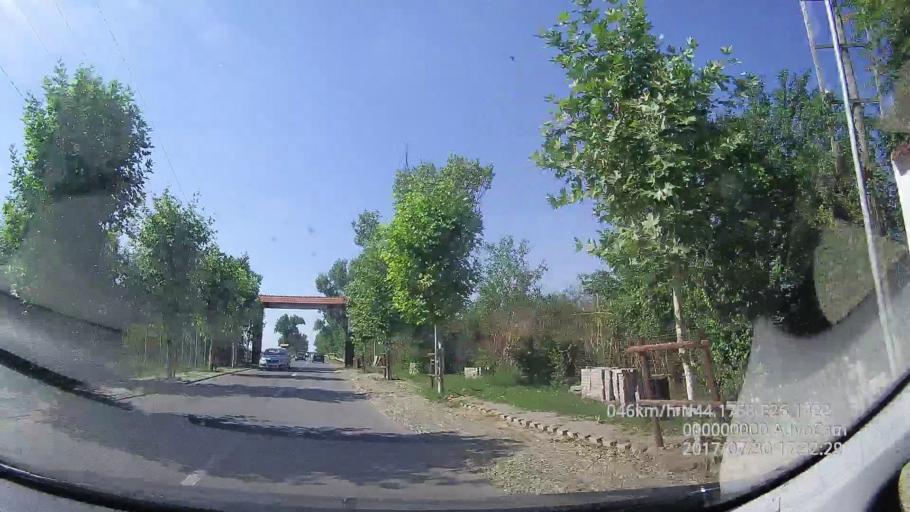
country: RO
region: Giurgiu
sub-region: Comuna Comana
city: Comana
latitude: 44.1771
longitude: 26.1419
